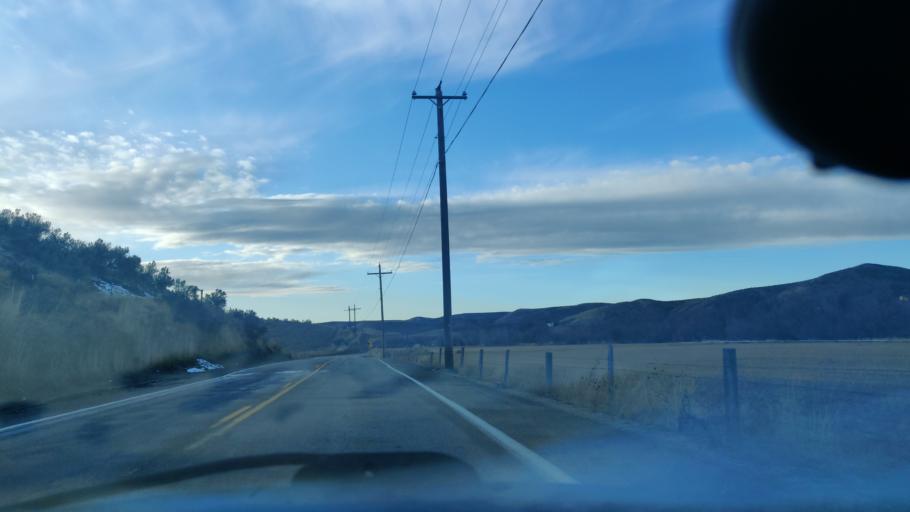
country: US
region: Idaho
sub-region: Ada County
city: Eagle
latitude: 43.7301
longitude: -116.2946
